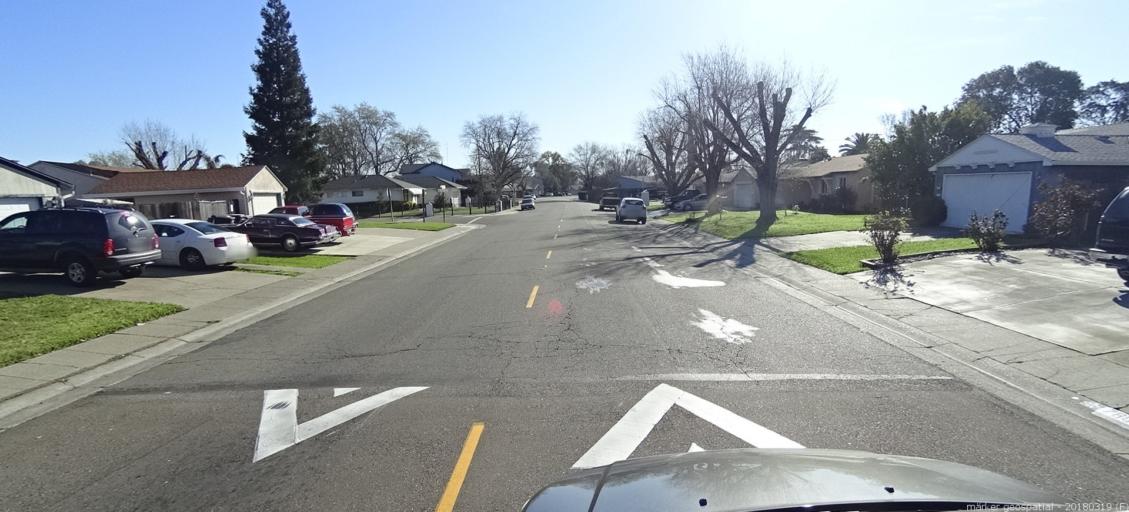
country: US
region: California
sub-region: Sacramento County
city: Parkway
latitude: 38.4856
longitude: -121.4493
